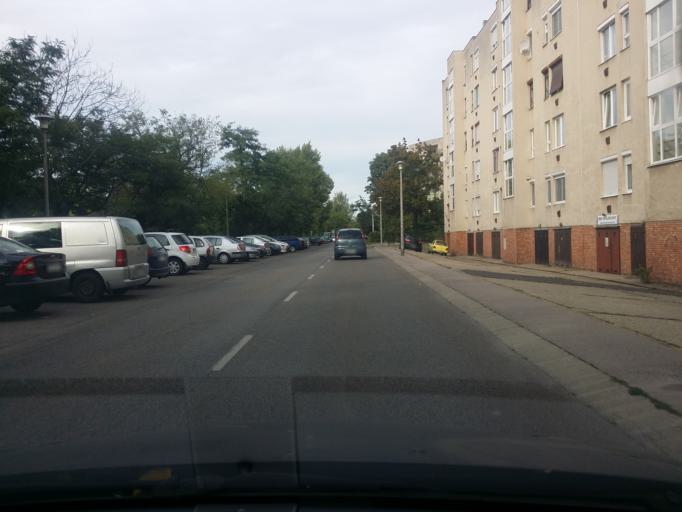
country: HU
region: Budapest
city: Budapest IV. keruelet
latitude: 47.5788
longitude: 19.0947
